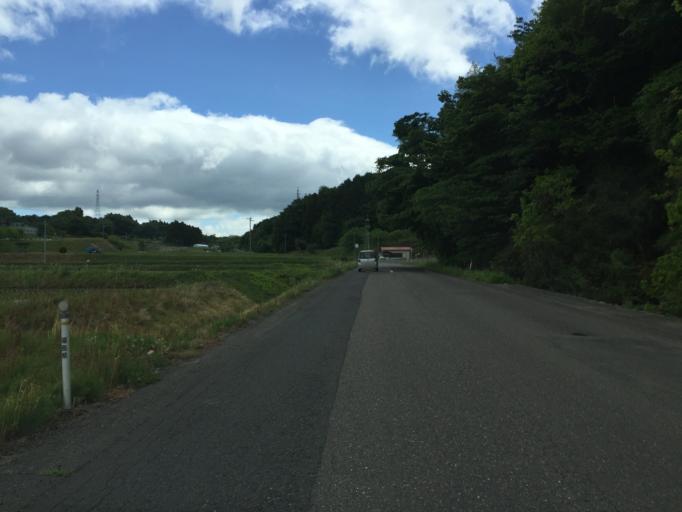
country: JP
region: Fukushima
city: Miharu
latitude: 37.4761
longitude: 140.4740
